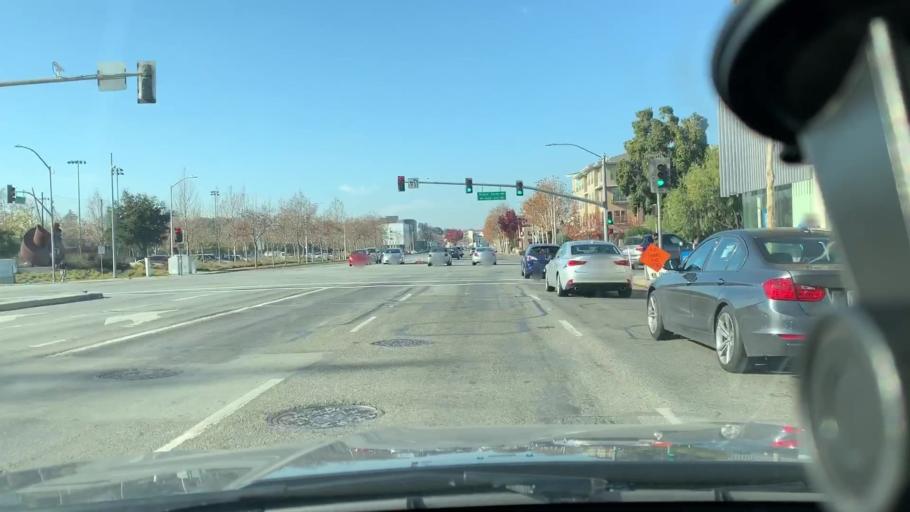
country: US
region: California
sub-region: Santa Clara County
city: Palo Alto
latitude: 37.4229
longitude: -122.1415
